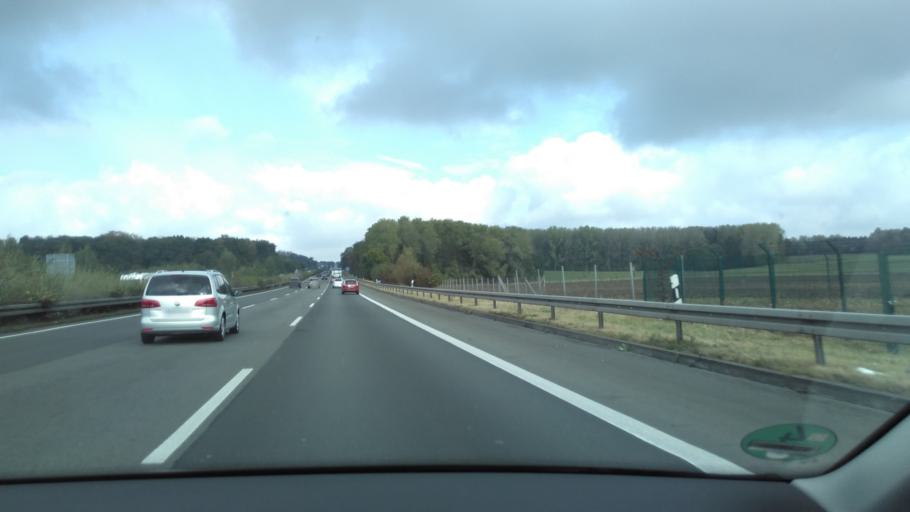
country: DE
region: North Rhine-Westphalia
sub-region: Regierungsbezirk Munster
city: Beckum
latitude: 51.7113
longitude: 7.9790
